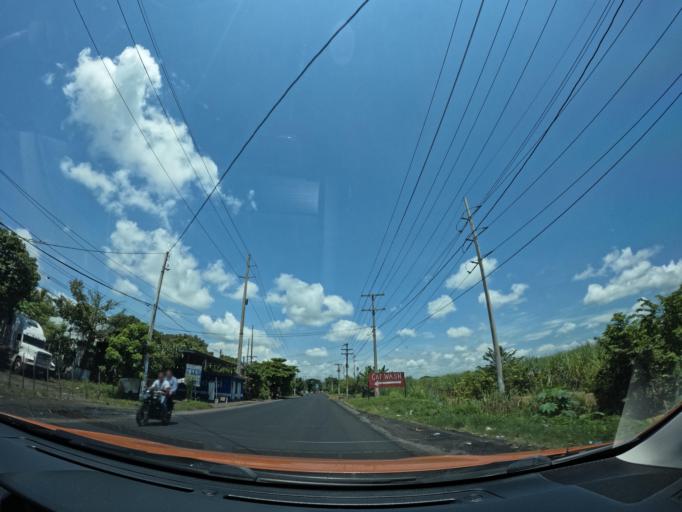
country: GT
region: Escuintla
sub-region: Municipio de Masagua
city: Masagua
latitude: 14.2096
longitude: -90.8396
